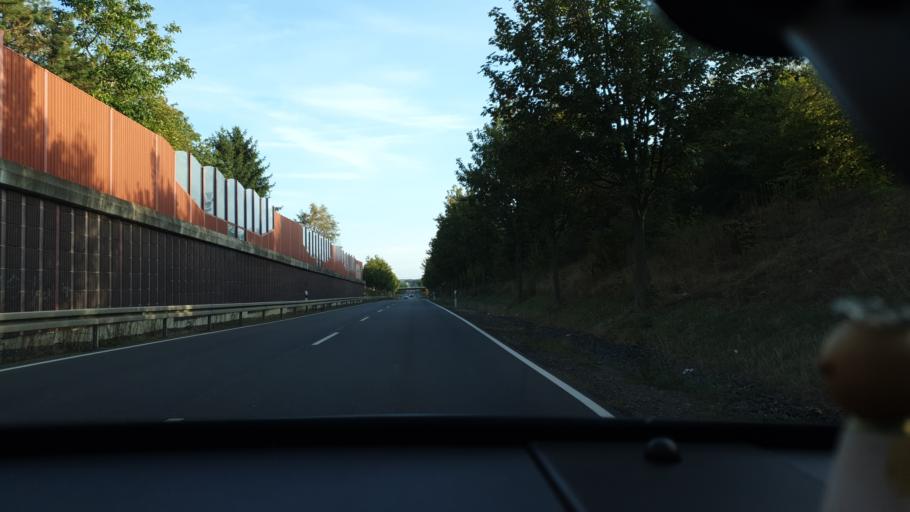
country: DE
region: Saxony
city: Eilenburg
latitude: 51.4540
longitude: 12.6121
